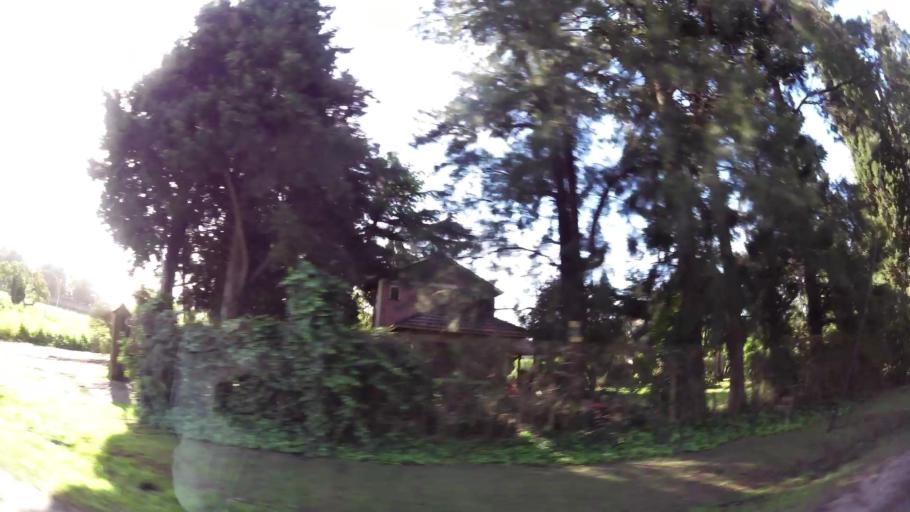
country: AR
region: Buenos Aires
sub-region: Partido de Quilmes
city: Quilmes
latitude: -34.8133
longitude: -58.2138
